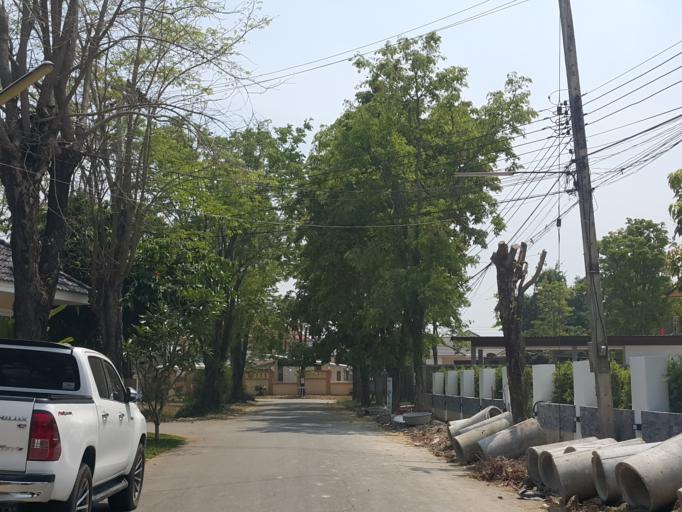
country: TH
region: Chiang Mai
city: Chiang Mai
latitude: 18.7300
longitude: 98.9740
